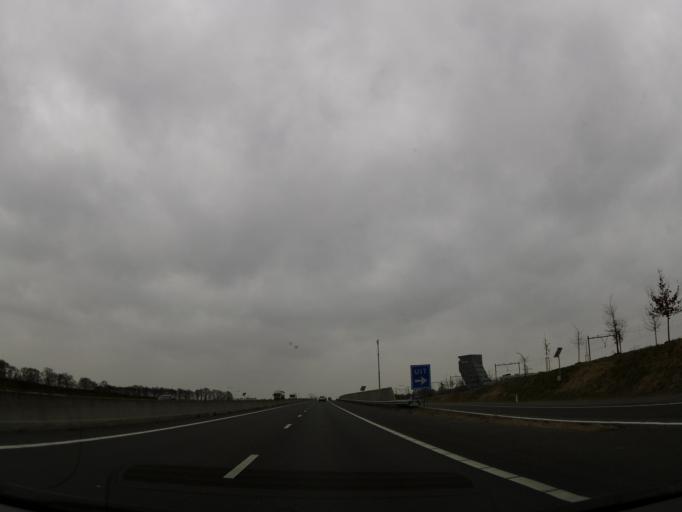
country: NL
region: Limburg
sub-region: Gemeente Roermond
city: Roermond
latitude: 51.1666
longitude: 5.9687
